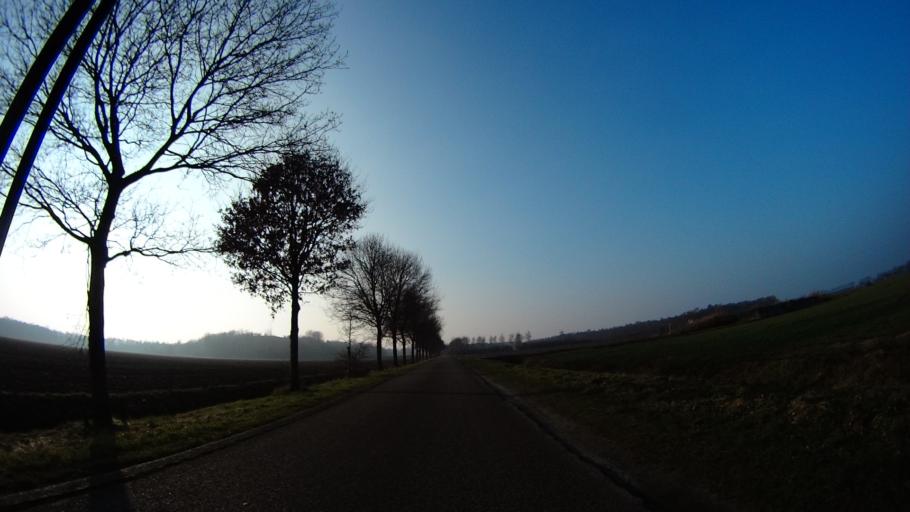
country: NL
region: Drenthe
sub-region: Gemeente Emmen
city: Emmen
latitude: 52.7951
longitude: 6.9642
